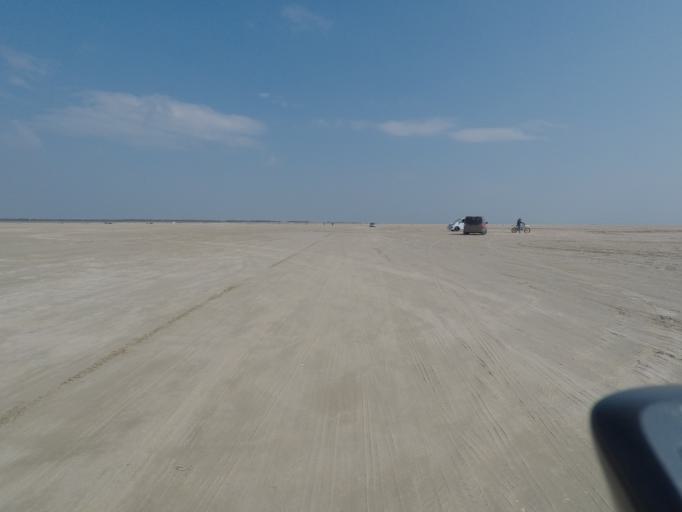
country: DE
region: Schleswig-Holstein
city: List
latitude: 55.0745
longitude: 8.4986
